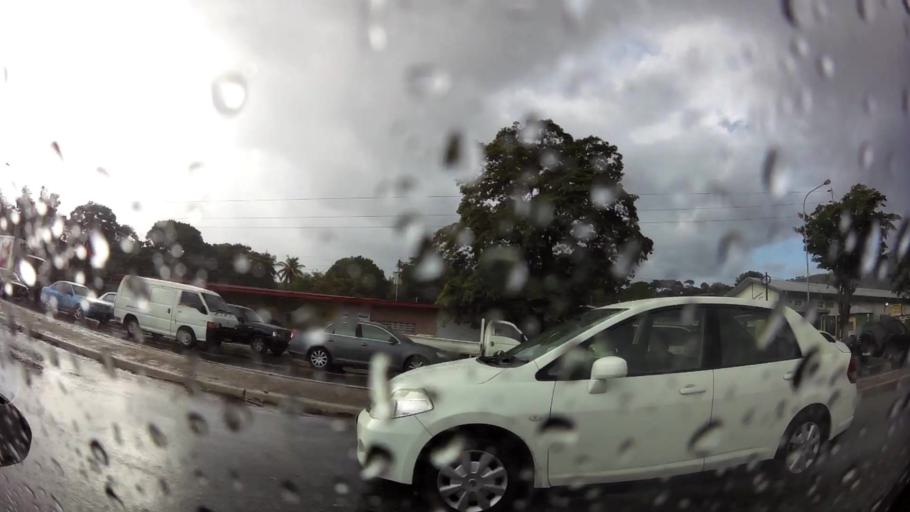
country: TT
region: Tunapuna/Piarco
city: Tunapuna
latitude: 10.6483
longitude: -61.4256
